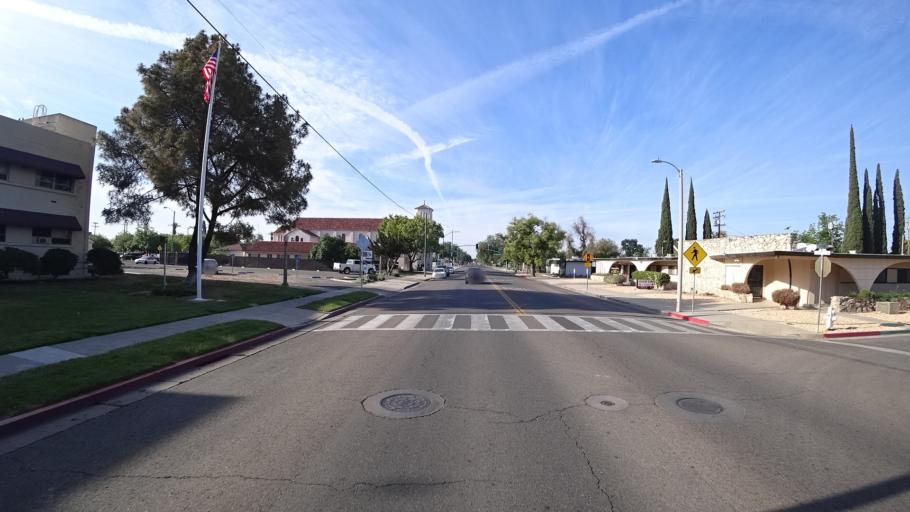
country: US
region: California
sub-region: Kings County
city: Hanford
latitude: 36.3359
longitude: -119.6461
